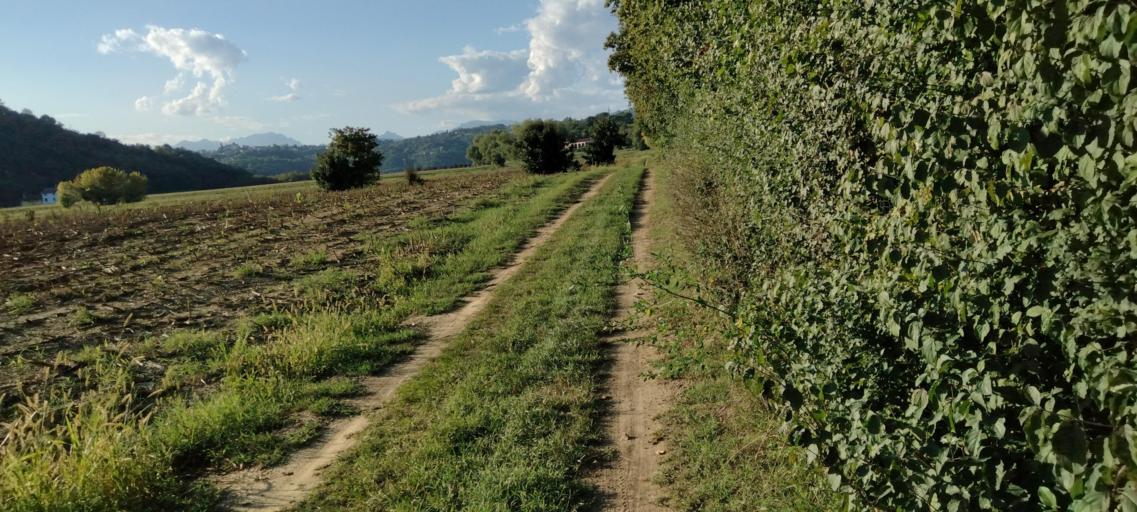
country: IT
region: Veneto
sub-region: Provincia di Vicenza
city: Creazzo
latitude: 45.5486
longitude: 11.4874
